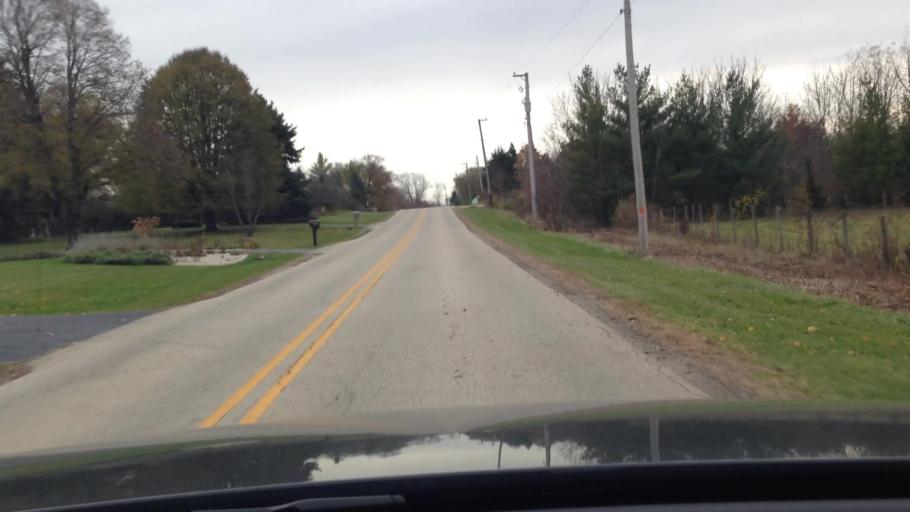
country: US
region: Illinois
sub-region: McHenry County
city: Woodstock
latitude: 42.2808
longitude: -88.4770
